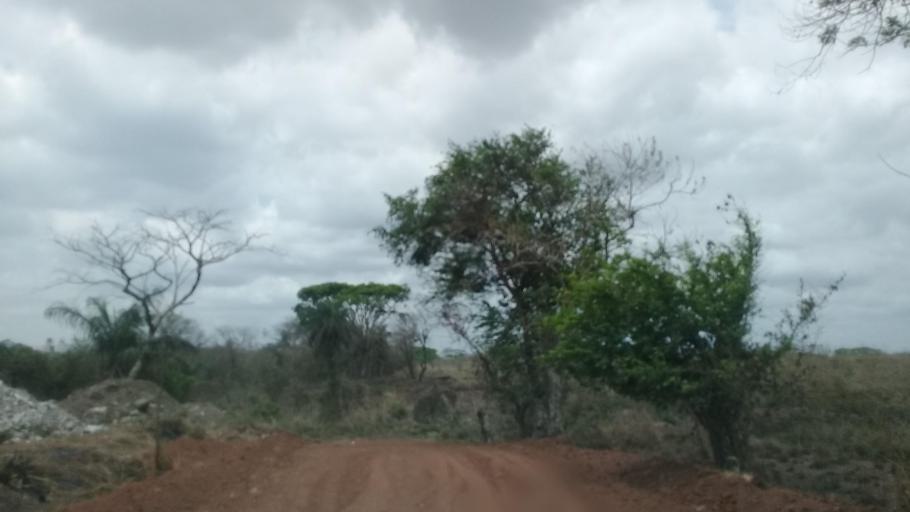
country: MX
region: Veracruz
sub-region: Veracruz
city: Las Amapolas
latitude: 19.1370
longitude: -96.2434
